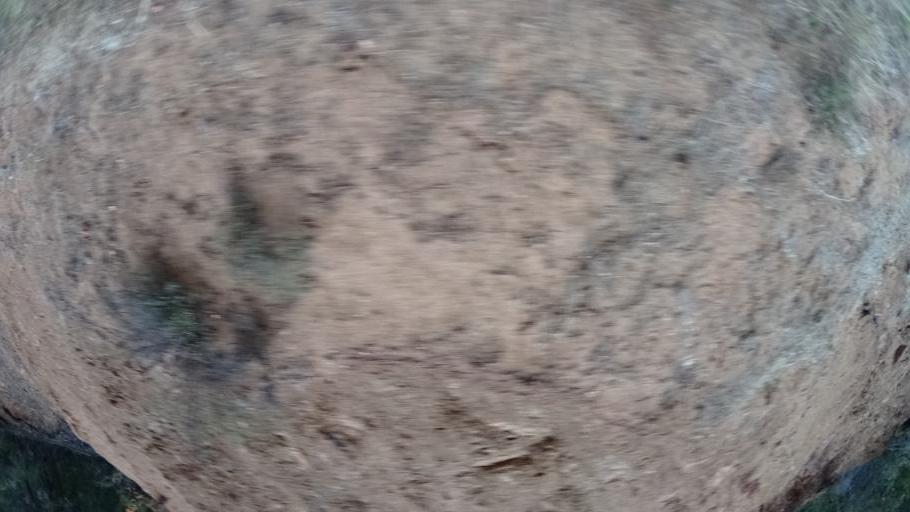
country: US
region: California
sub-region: Siskiyou County
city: Happy Camp
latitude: 41.8957
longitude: -123.4344
